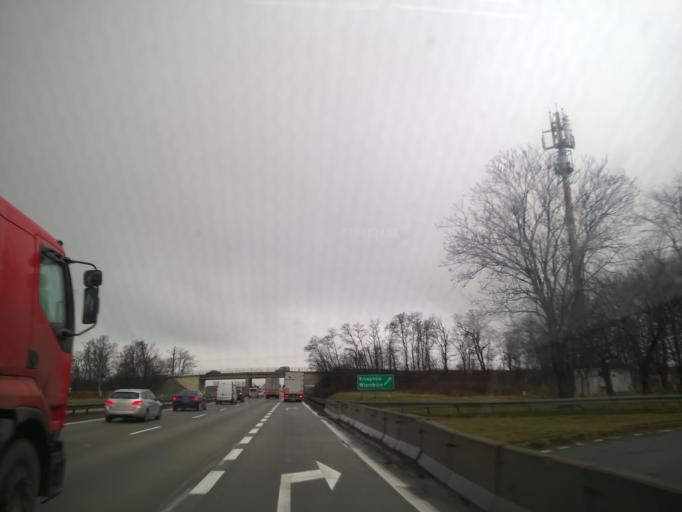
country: PL
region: Lower Silesian Voivodeship
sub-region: Powiat wroclawski
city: Tyniec Maly
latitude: 51.0383
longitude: 16.8957
